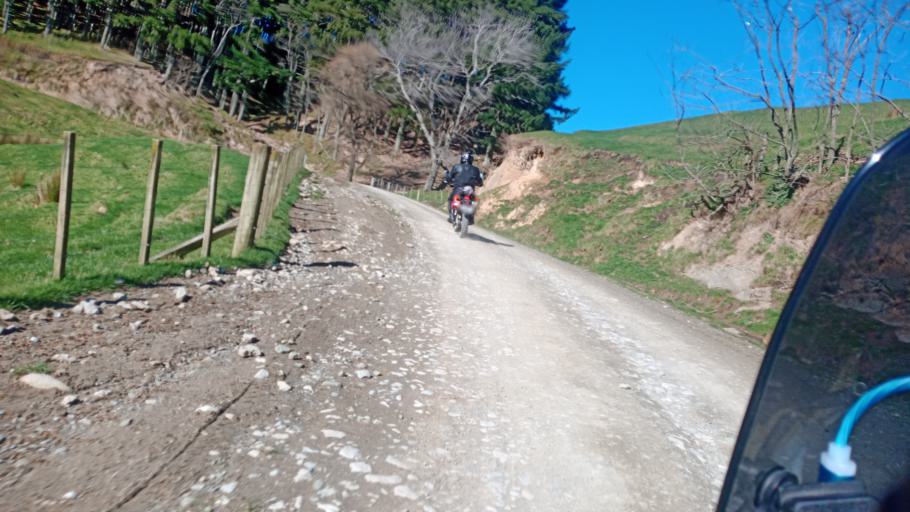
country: NZ
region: Gisborne
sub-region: Gisborne District
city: Gisborne
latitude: -38.2910
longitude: 177.8732
